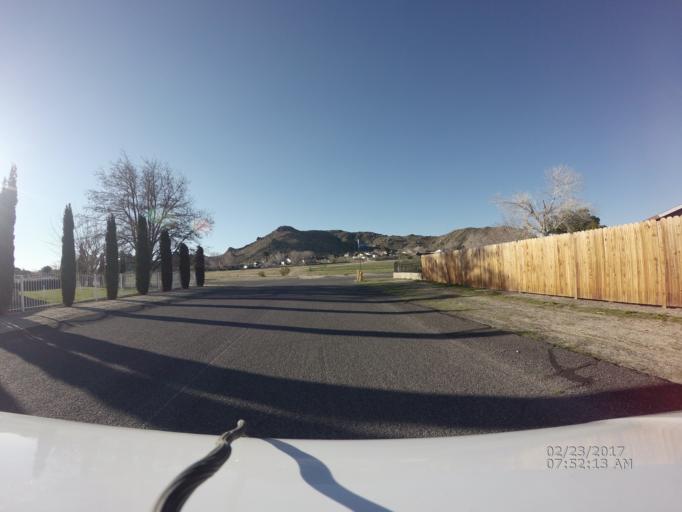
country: US
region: California
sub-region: Los Angeles County
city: Lake Los Angeles
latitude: 34.6106
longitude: -117.8154
